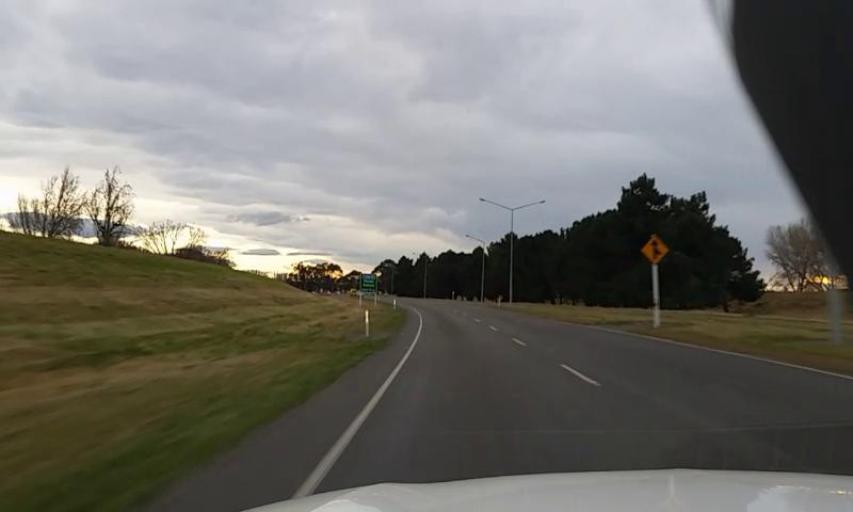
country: NZ
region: Canterbury
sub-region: Waimakariri District
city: Kaiapoi
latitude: -43.4285
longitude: 172.6461
